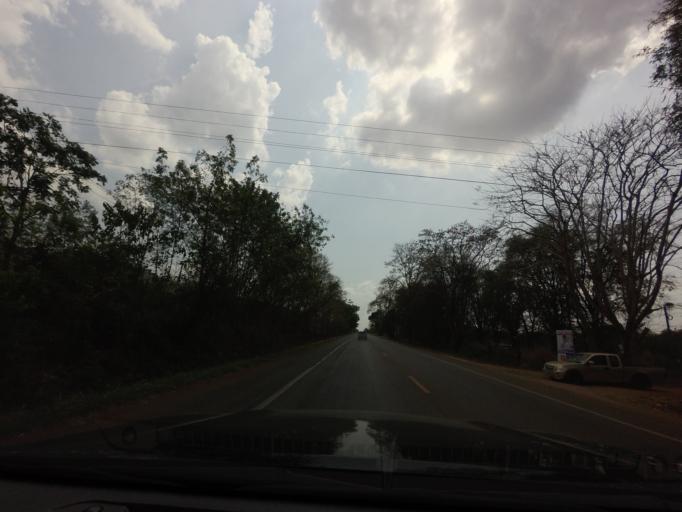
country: TH
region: Kanchanaburi
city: Sai Yok
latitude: 14.1574
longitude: 99.1389
